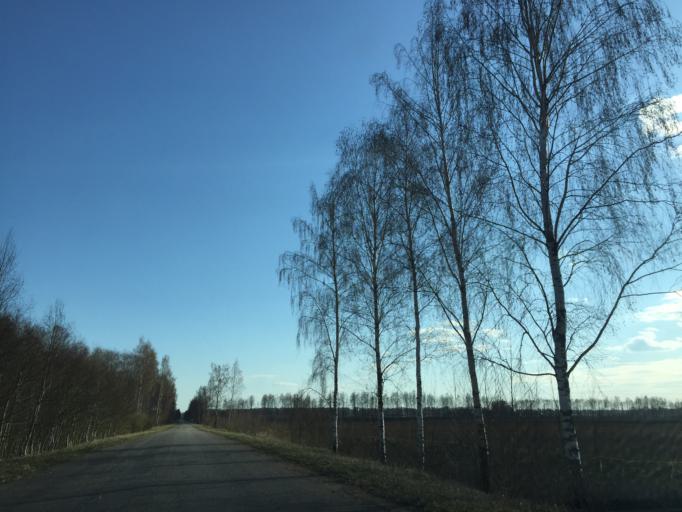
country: EE
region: Valgamaa
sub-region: Torva linn
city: Torva
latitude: 58.2487
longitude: 25.9500
